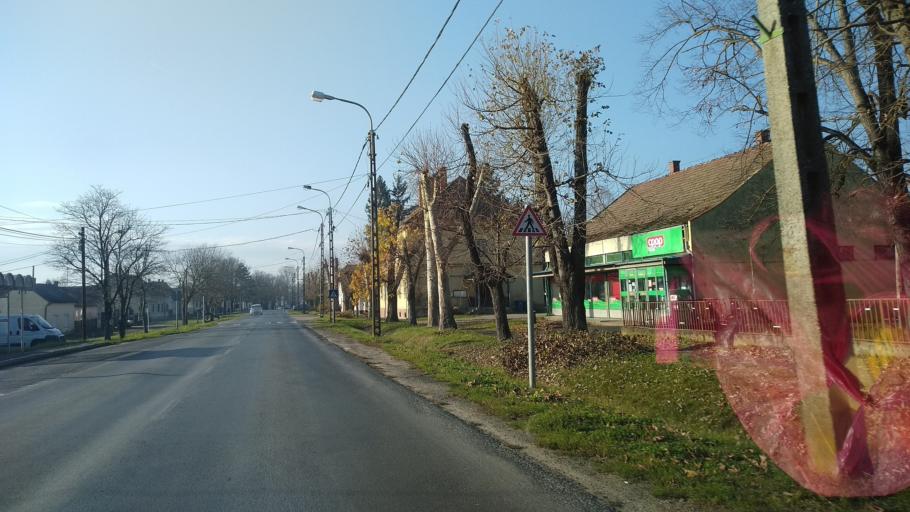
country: HU
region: Somogy
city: Barcs
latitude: 45.9596
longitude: 17.4743
